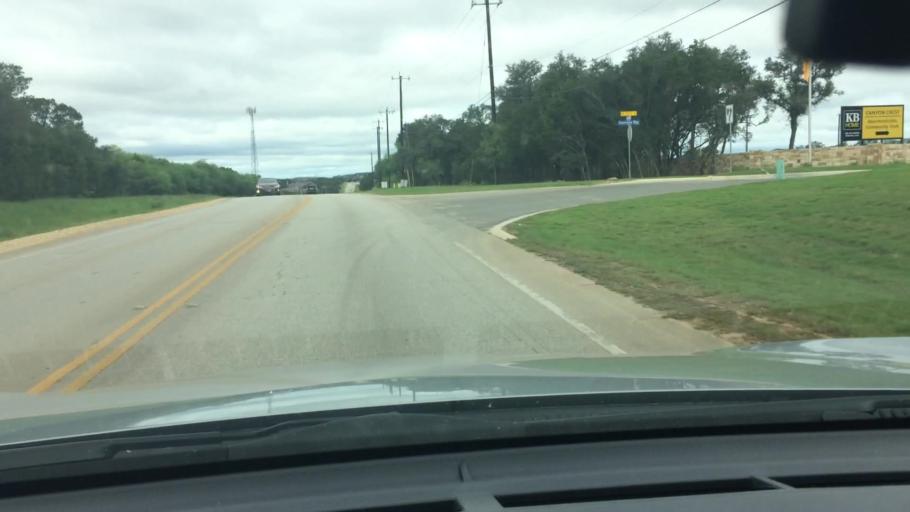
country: US
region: Texas
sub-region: Comal County
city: Garden Ridge
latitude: 29.6426
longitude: -98.3885
